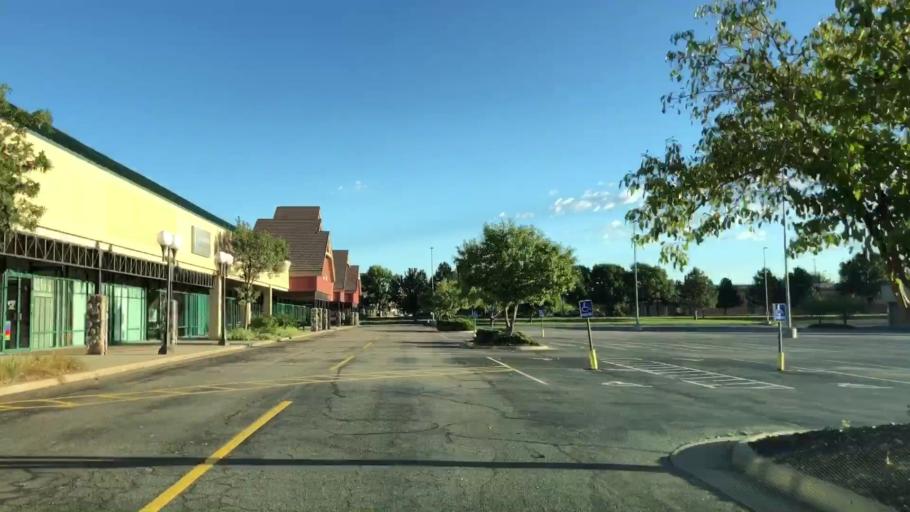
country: US
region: Colorado
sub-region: Larimer County
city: Loveland
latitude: 40.4094
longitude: -104.9967
